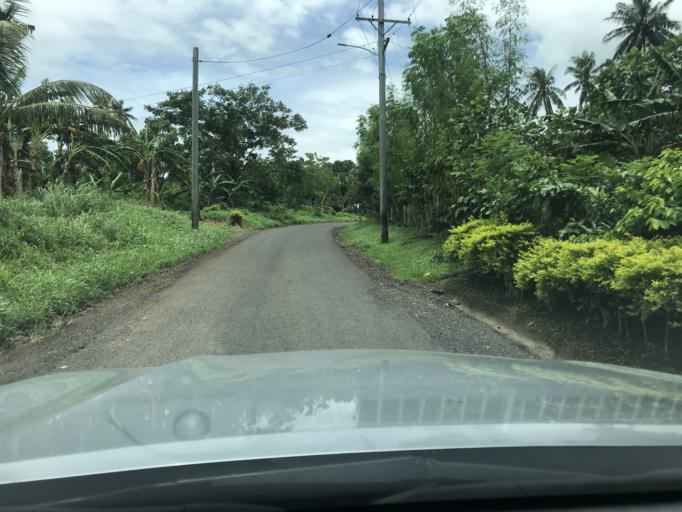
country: WS
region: Tuamasaga
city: Afenga
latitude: -13.8058
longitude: -171.8863
